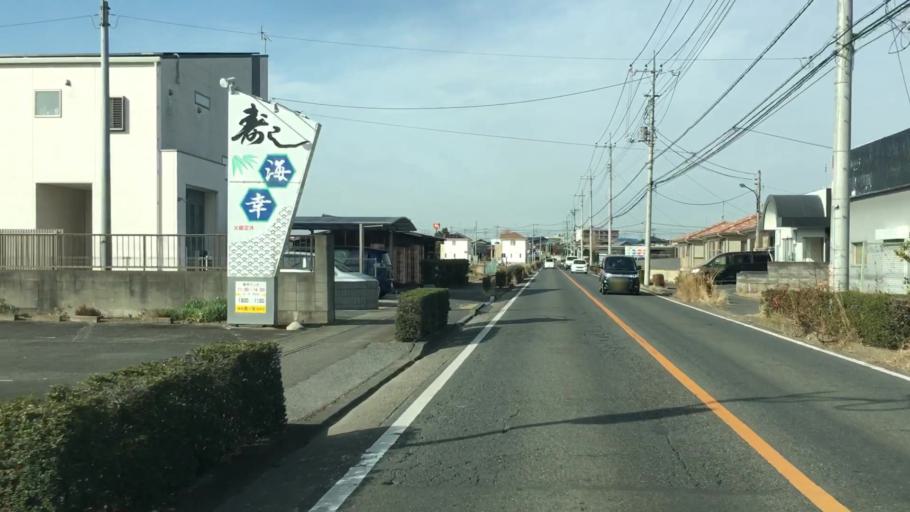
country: JP
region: Saitama
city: Menuma
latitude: 36.2537
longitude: 139.4221
